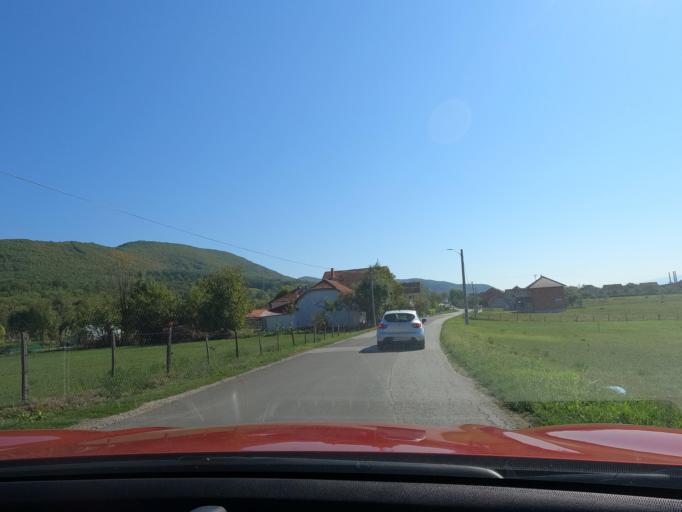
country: RS
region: Central Serbia
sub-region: Raski Okrug
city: Kraljevo
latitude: 43.7488
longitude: 20.7141
